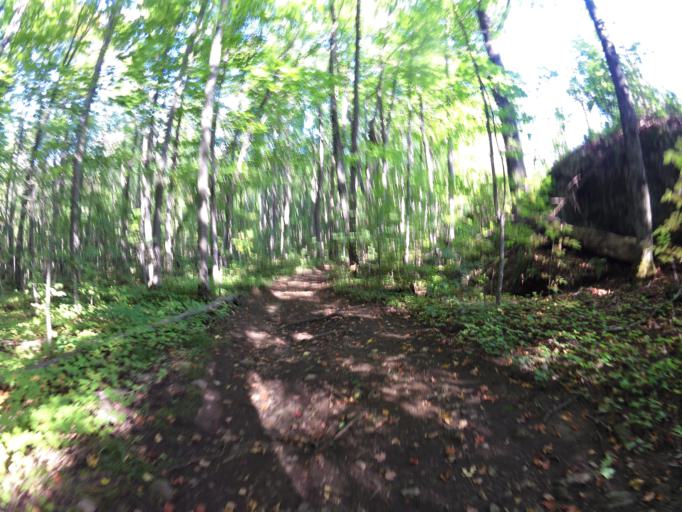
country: CA
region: Ontario
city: Bells Corners
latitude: 45.3397
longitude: -75.9347
